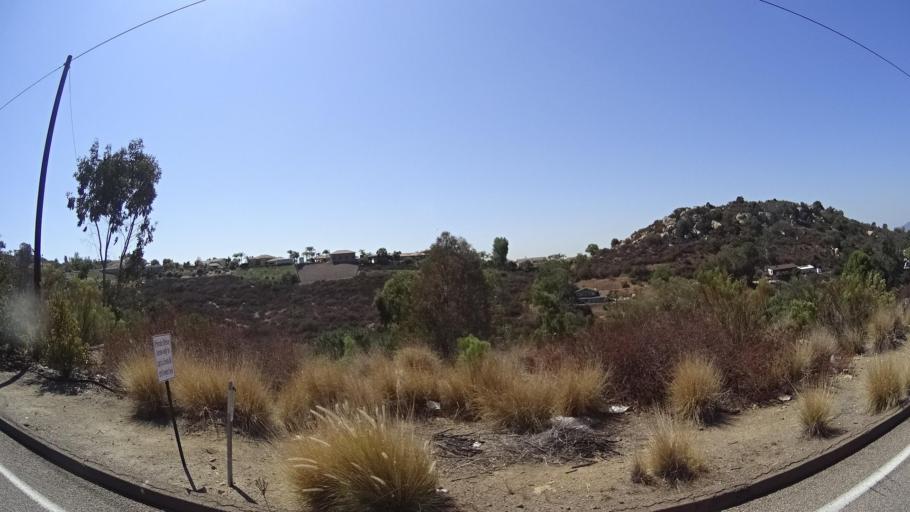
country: US
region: California
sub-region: San Diego County
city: Granite Hills
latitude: 32.8095
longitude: -116.8980
